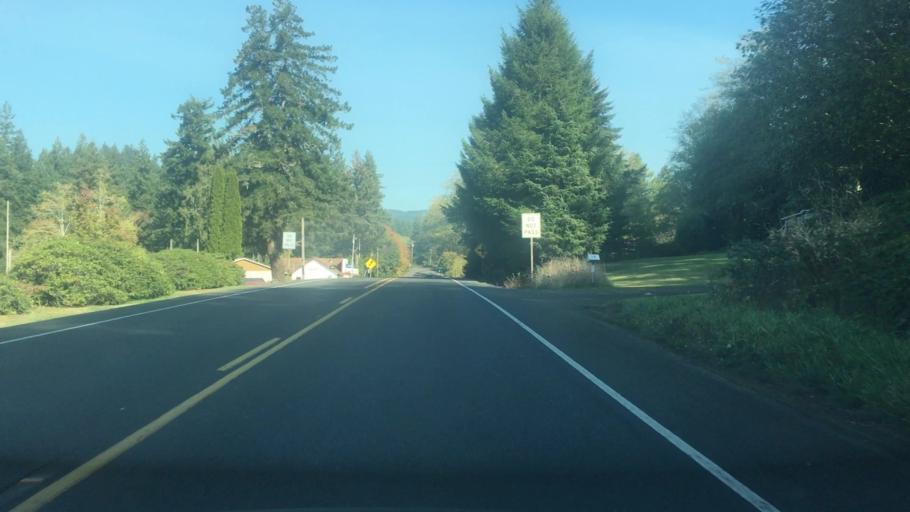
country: US
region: Oregon
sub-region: Lincoln County
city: Rose Lodge
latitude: 45.0091
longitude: -123.8827
